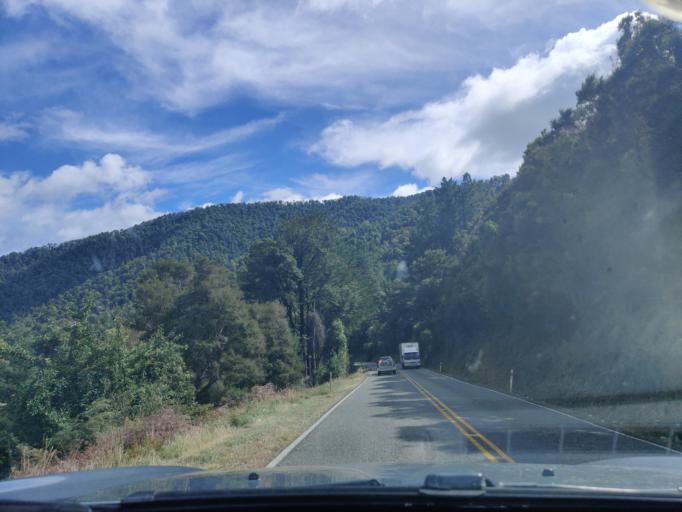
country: NZ
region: Tasman
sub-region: Tasman District
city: Wakefield
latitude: -41.6943
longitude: 172.4960
